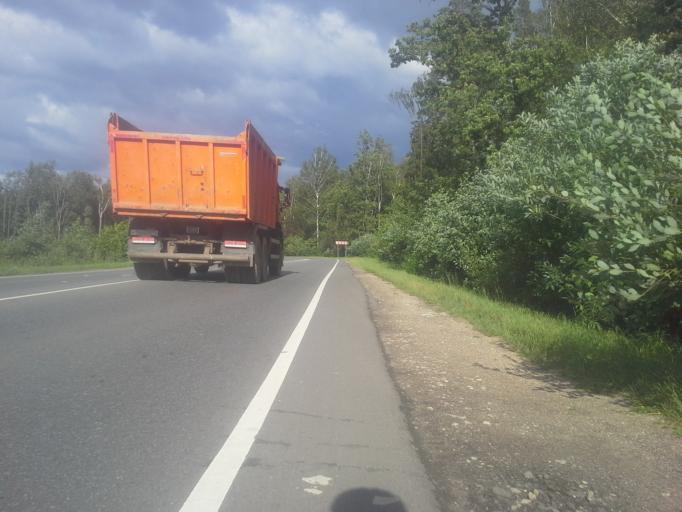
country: RU
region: Moskovskaya
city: Zvenigorod
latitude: 55.7035
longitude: 36.8390
